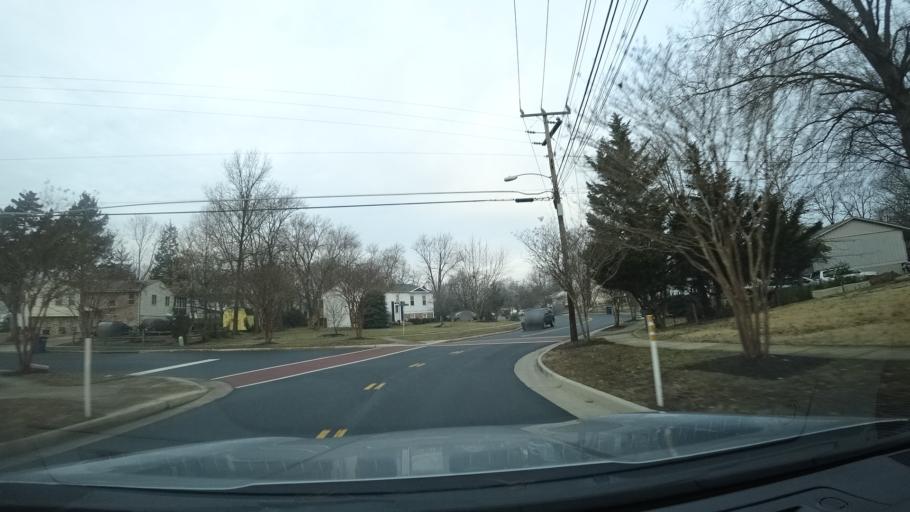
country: US
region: Virginia
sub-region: Fairfax County
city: Herndon
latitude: 38.9612
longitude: -77.3878
